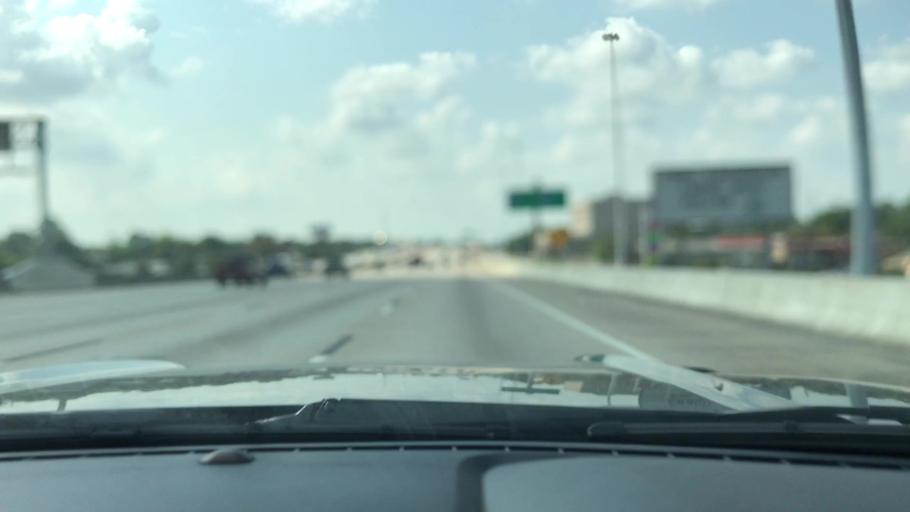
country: US
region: Texas
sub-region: Harris County
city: Houston
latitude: 29.8474
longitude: -95.3337
